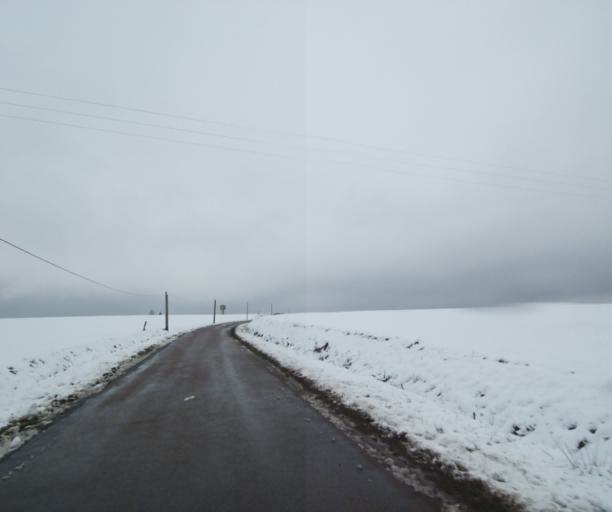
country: FR
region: Champagne-Ardenne
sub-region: Departement de la Haute-Marne
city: Laneuville-a-Remy
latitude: 48.5087
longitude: 4.8493
